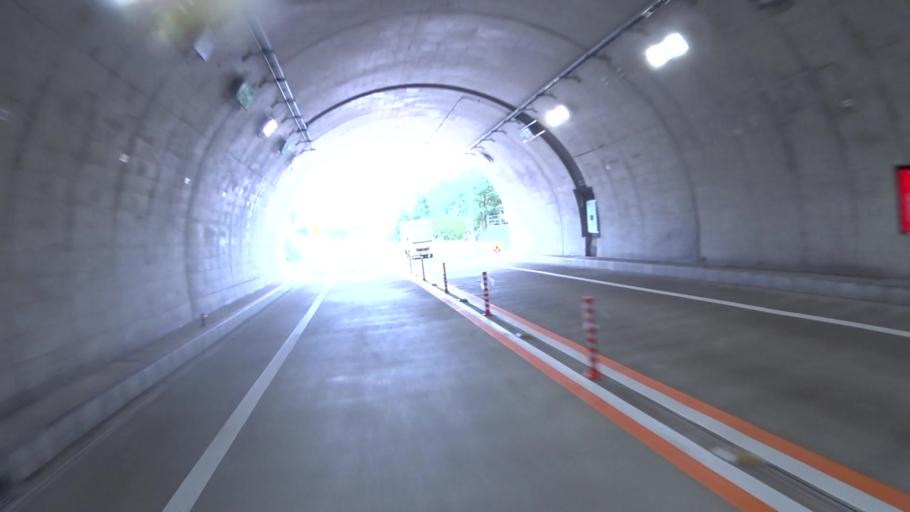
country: JP
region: Kyoto
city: Ayabe
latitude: 35.2693
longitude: 135.3446
